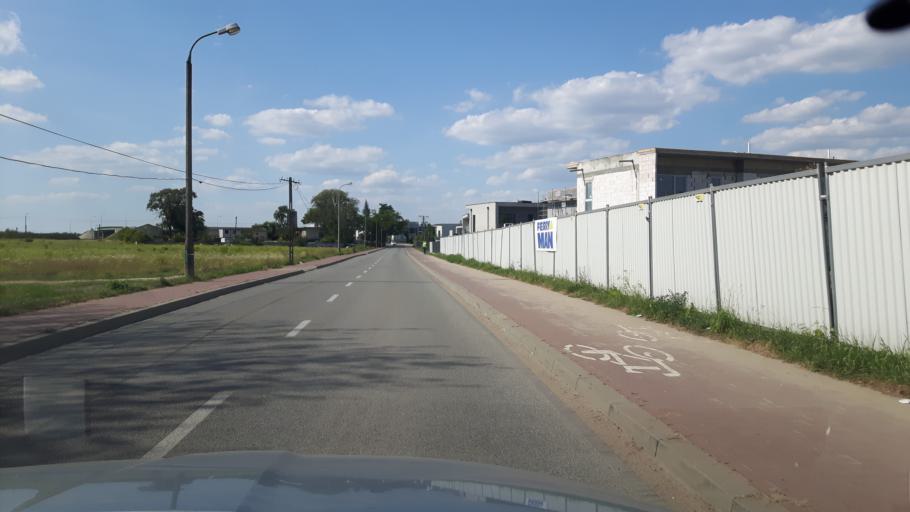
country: PL
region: Masovian Voivodeship
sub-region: Powiat pruszkowski
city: Nowe Grocholice
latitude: 52.1619
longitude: 20.9133
